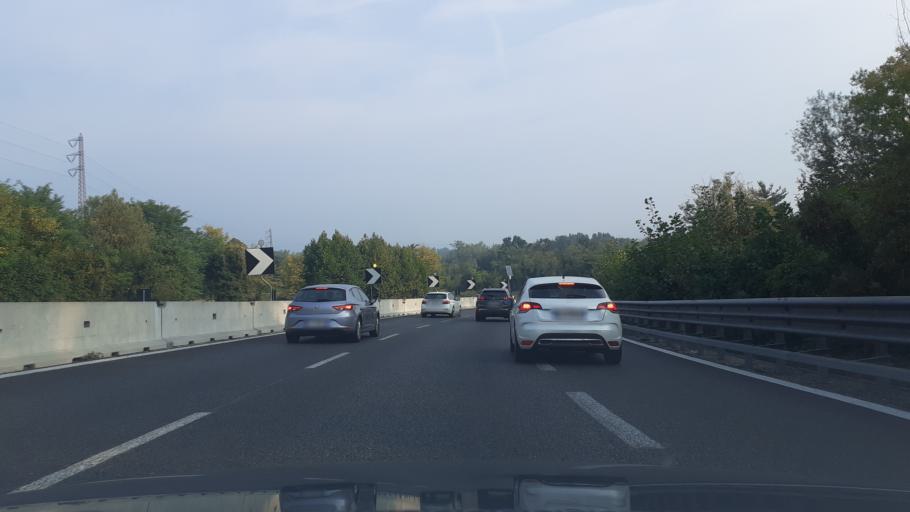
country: IT
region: Lombardy
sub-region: Provincia di Monza e Brianza
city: Briosco
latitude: 45.7142
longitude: 9.2274
